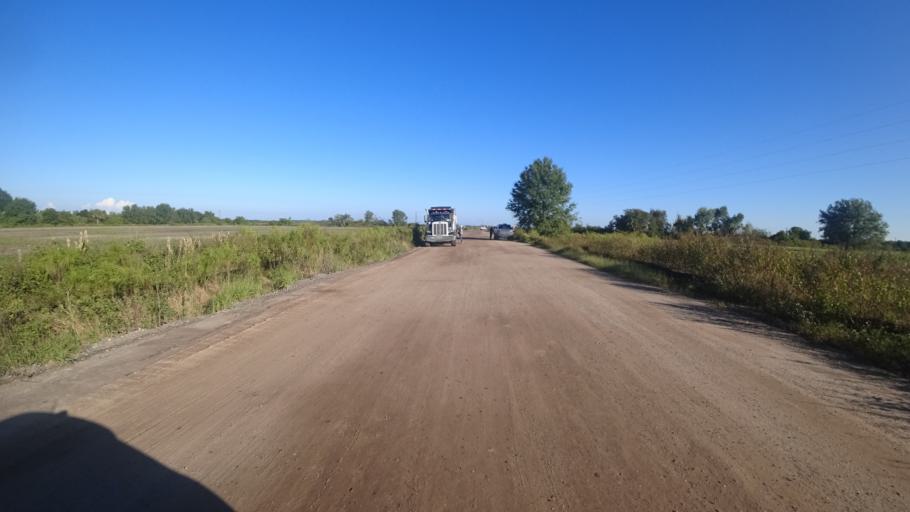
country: US
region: Florida
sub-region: Hillsborough County
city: Ruskin
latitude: 27.6290
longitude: -82.4885
